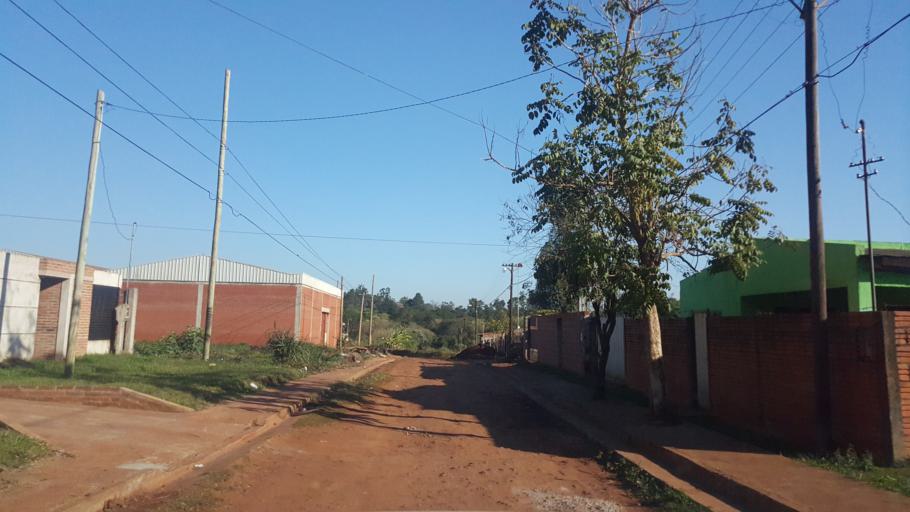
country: AR
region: Misiones
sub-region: Departamento de Capital
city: Posadas
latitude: -27.4077
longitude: -55.9380
